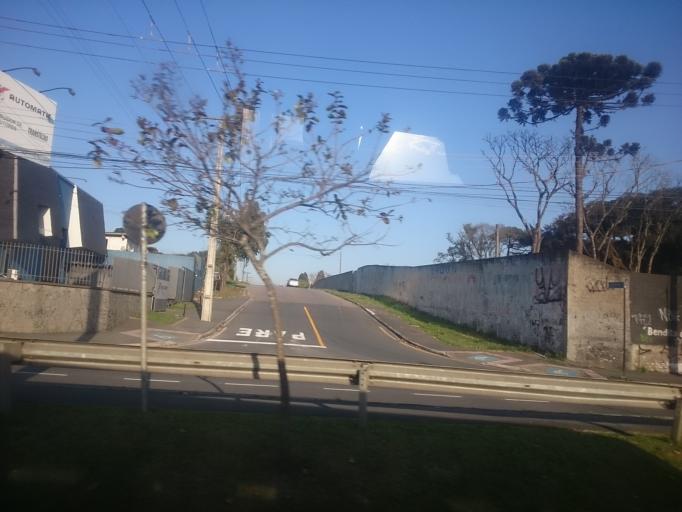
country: BR
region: Parana
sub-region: Curitiba
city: Curitiba
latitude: -25.4987
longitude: -49.2776
